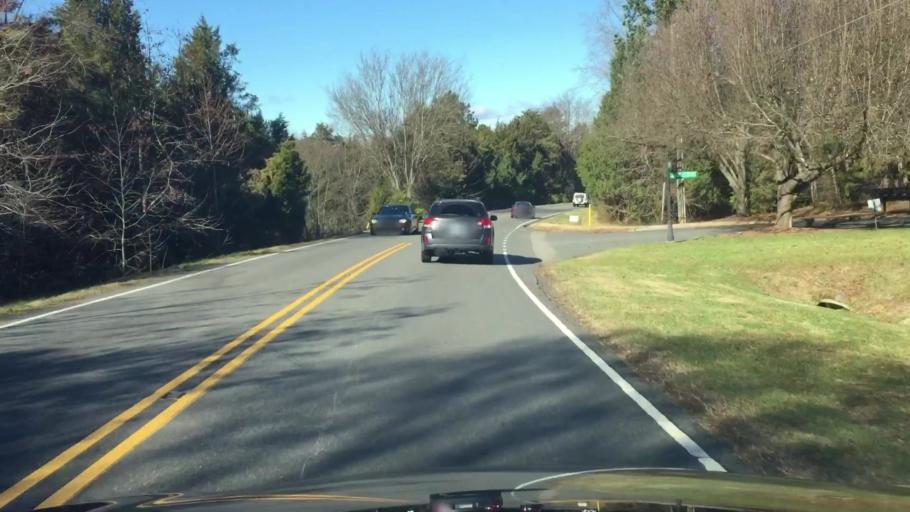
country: US
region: North Carolina
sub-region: Iredell County
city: Mooresville
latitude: 35.5603
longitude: -80.8648
